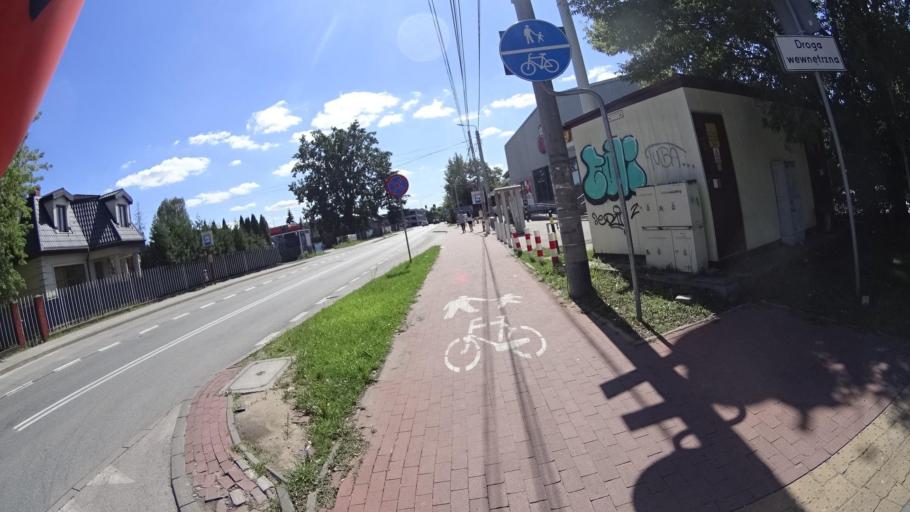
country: PL
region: Masovian Voivodeship
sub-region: Powiat piaseczynski
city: Jozefoslaw
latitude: 52.0854
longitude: 21.0451
